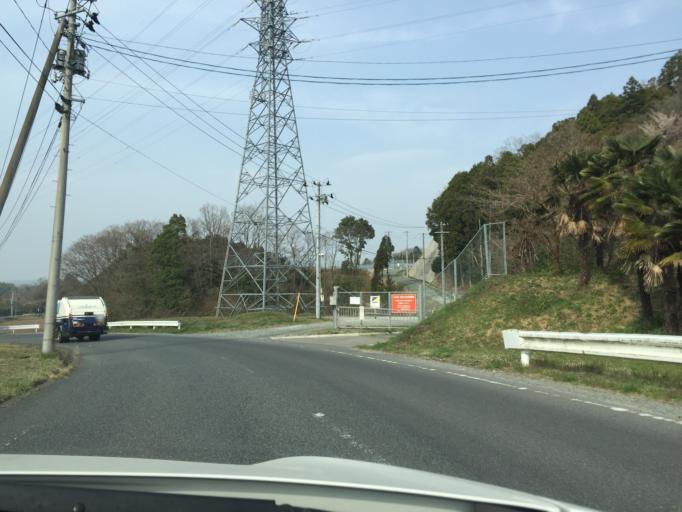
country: JP
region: Fukushima
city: Iwaki
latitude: 36.9724
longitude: 140.8548
